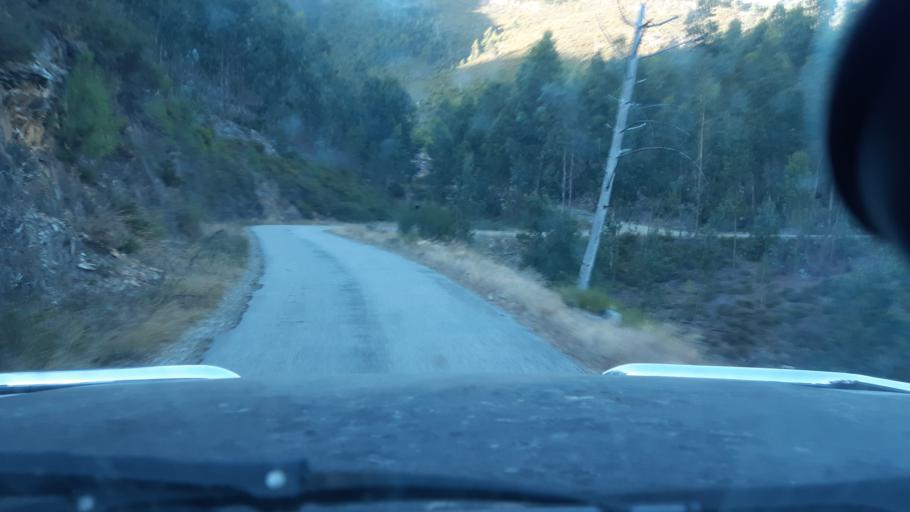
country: PT
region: Viseu
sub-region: Mortagua
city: Mortagua
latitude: 40.5322
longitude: -8.2525
